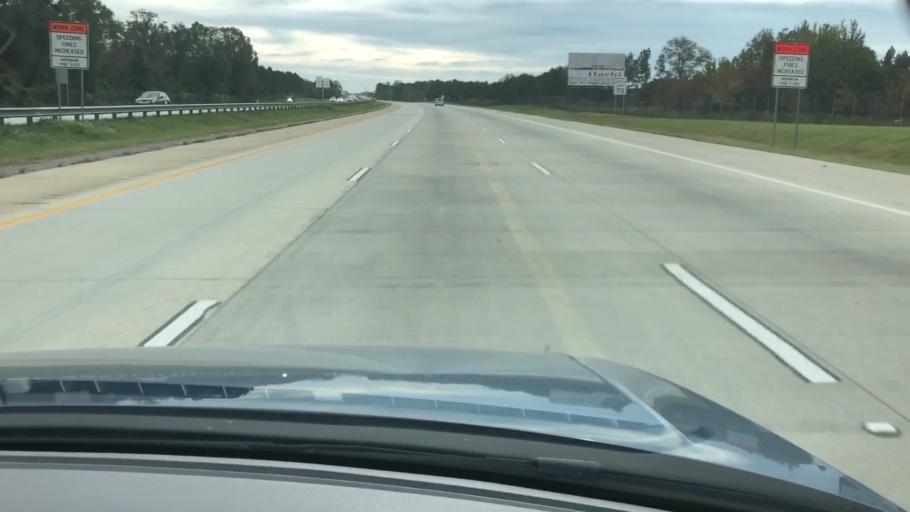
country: US
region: Georgia
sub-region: Dooly County
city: Vienna
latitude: 32.1127
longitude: -83.7632
